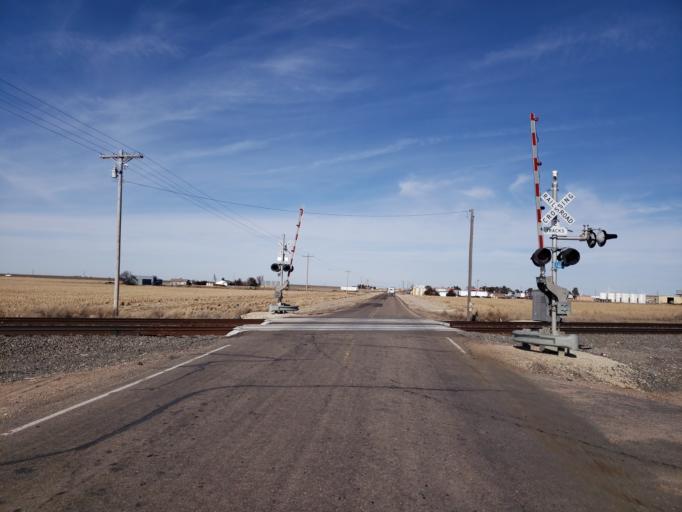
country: US
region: Kansas
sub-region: Ford County
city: Dodge City
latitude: 37.7747
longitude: -99.9059
